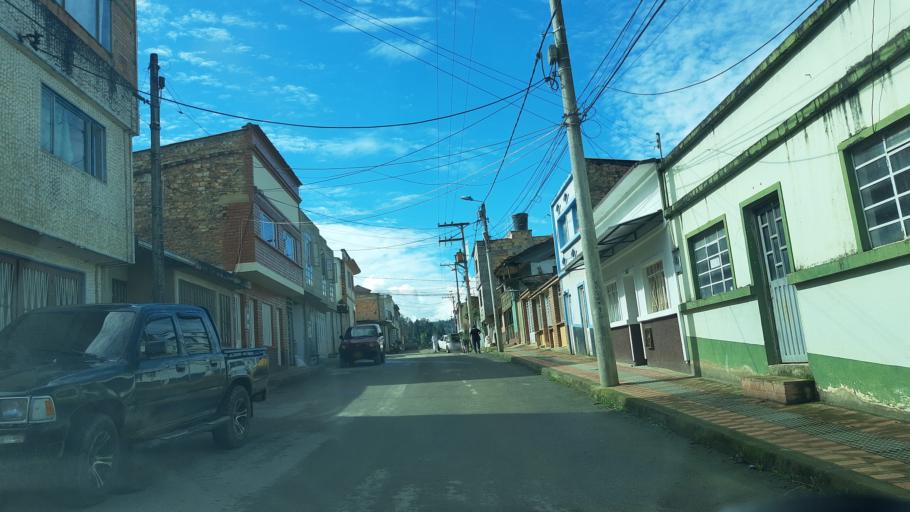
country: CO
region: Boyaca
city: Garagoa
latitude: 5.0825
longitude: -73.3613
